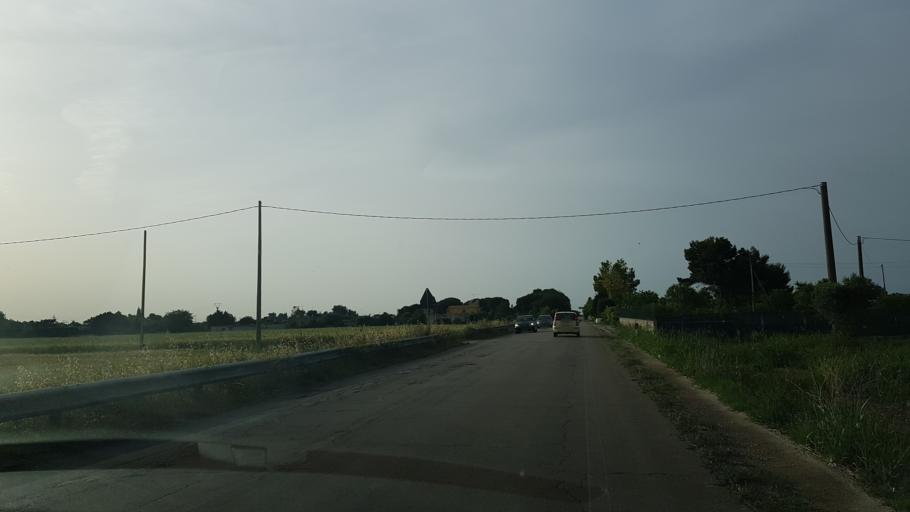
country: IT
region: Apulia
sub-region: Provincia di Brindisi
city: Tuturano
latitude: 40.5432
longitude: 17.9783
